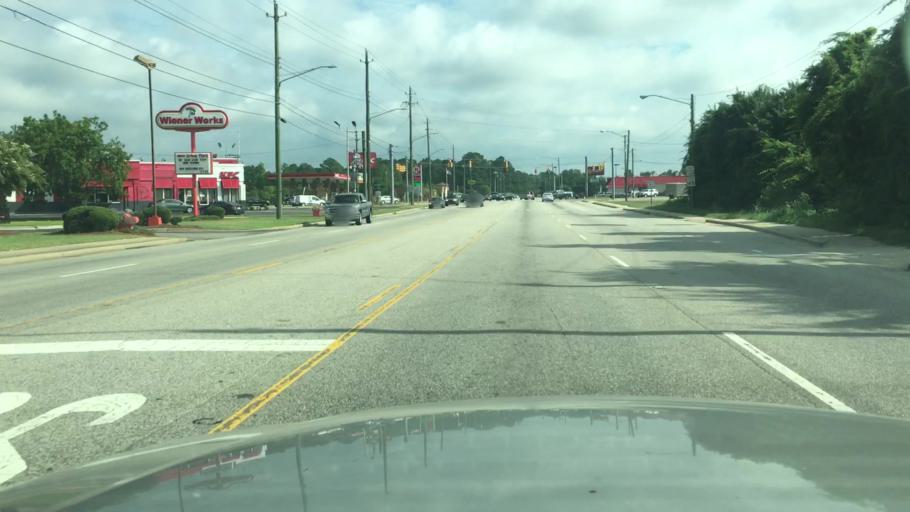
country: US
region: North Carolina
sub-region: Cumberland County
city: Hope Mills
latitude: 35.0036
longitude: -78.9671
